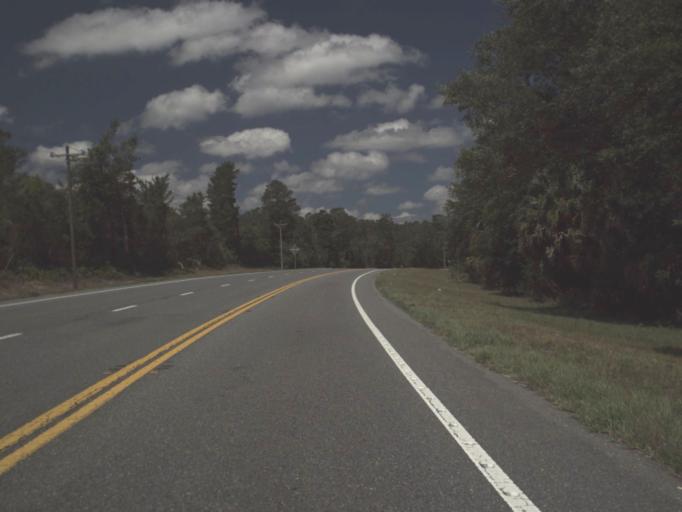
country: US
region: Florida
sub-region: Lake County
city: Astor
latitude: 29.1740
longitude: -81.6884
